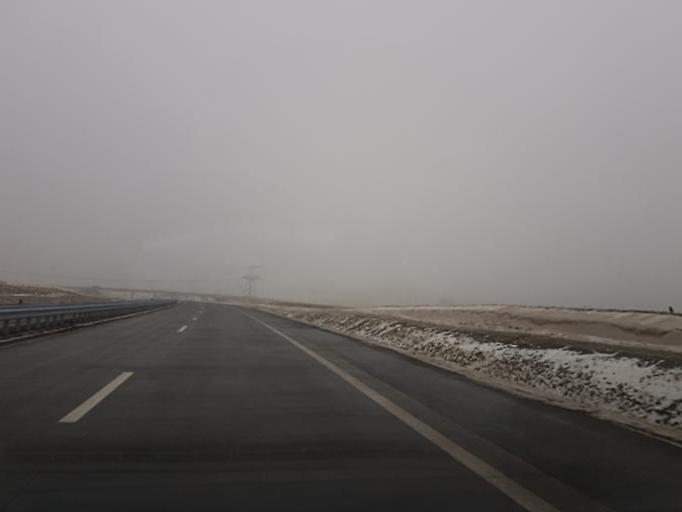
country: BY
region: Minsk
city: Atolina
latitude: 53.7608
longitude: 27.3999
